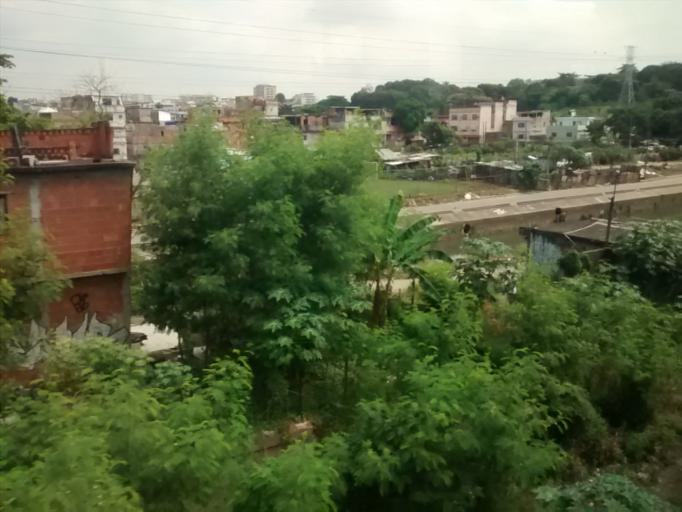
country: BR
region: Rio de Janeiro
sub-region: Rio De Janeiro
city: Rio de Janeiro
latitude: -22.8764
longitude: -43.2522
